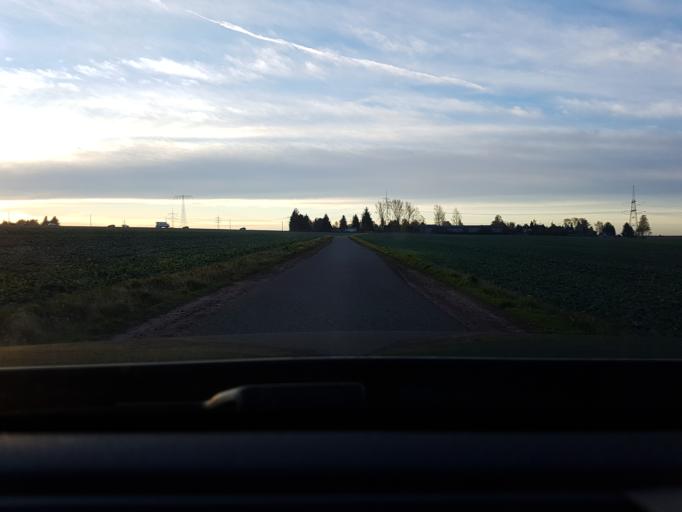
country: DE
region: Saxony
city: Altmittweida
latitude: 50.9560
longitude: 12.9694
